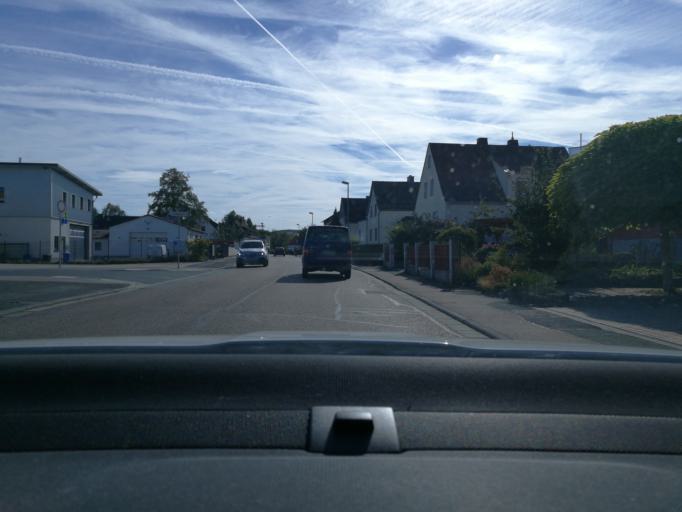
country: DE
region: Hesse
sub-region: Regierungsbezirk Giessen
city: Steeden
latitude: 50.3722
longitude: 8.1204
